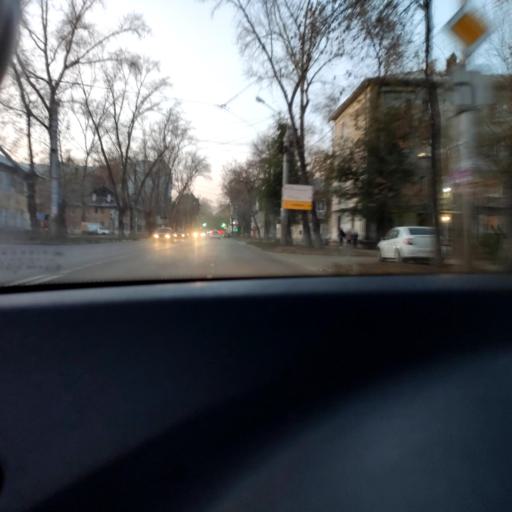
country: RU
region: Samara
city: Samara
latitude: 53.2267
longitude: 50.2570
